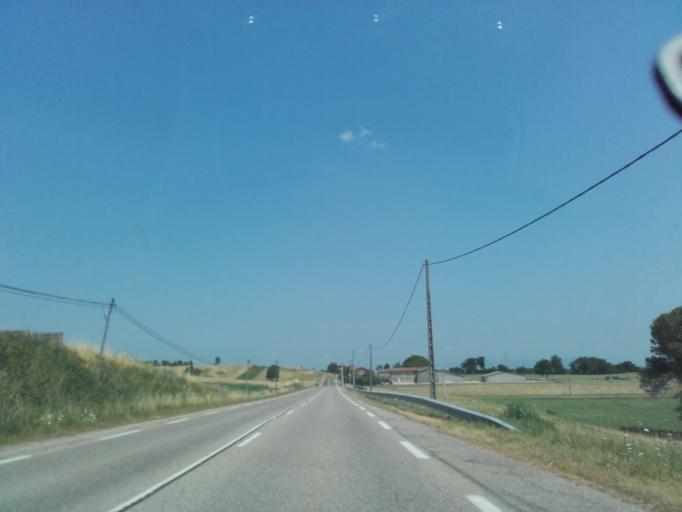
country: FR
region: Rhone-Alpes
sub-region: Departement de l'Isere
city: Champier
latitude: 45.4869
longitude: 5.2941
